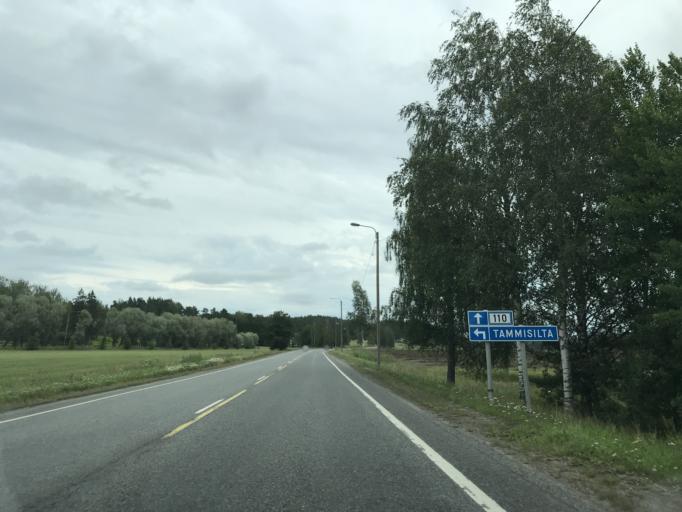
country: FI
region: Varsinais-Suomi
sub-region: Turku
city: Piikkioe
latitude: 60.4311
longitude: 22.5588
